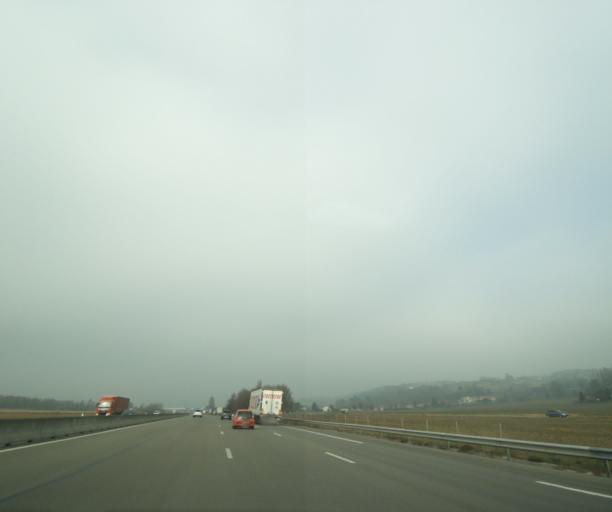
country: FR
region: Rhone-Alpes
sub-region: Departement de l'Isere
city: Reventin-Vaugris
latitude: 45.4671
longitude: 4.8333
